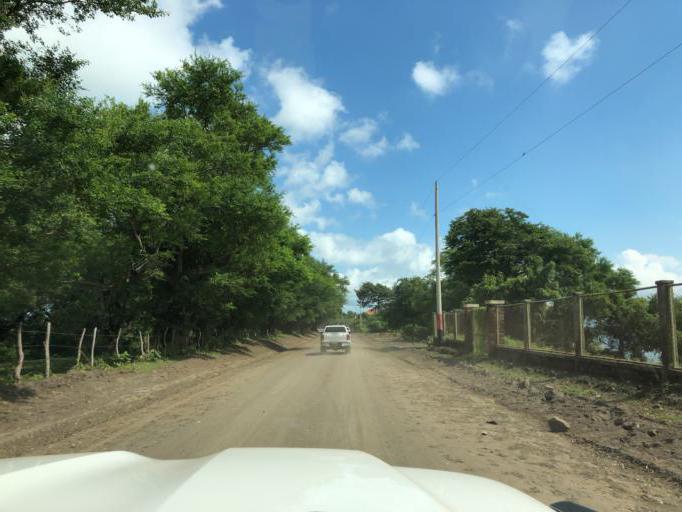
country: NI
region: Granada
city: Granada
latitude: 12.0071
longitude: -85.9330
